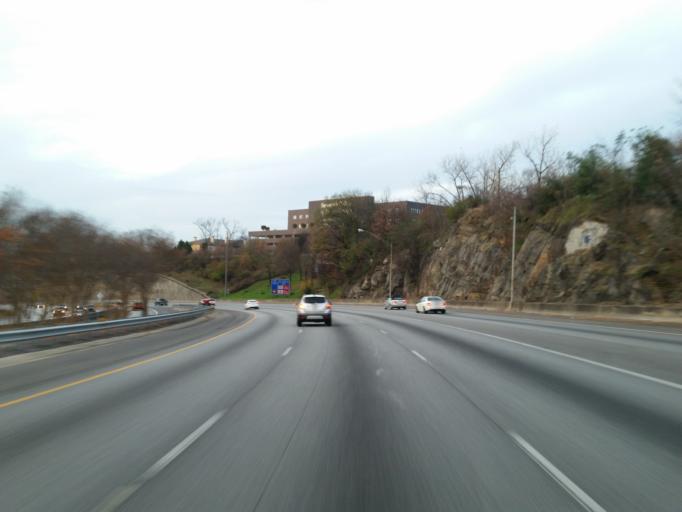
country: US
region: Georgia
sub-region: Fulton County
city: Atlanta
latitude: 33.7934
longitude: -84.3908
